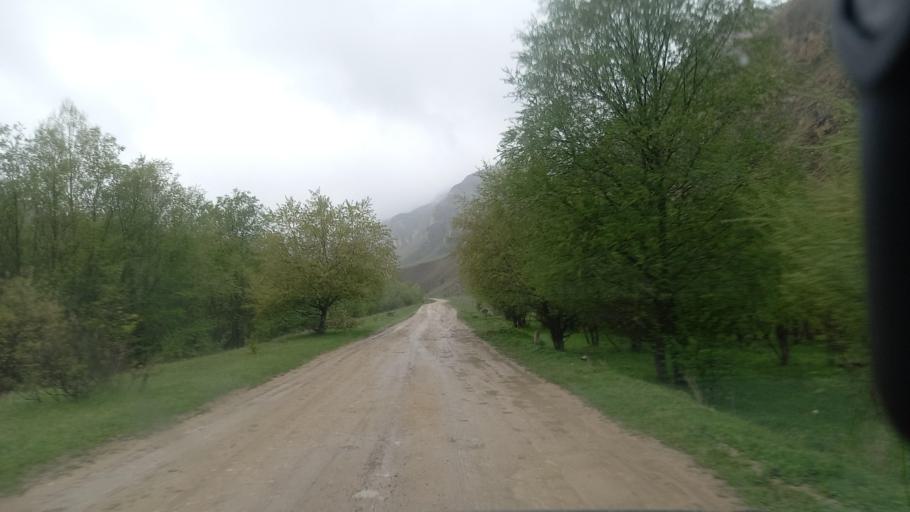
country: RU
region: Kabardino-Balkariya
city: Gundelen
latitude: 43.5978
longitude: 43.0625
